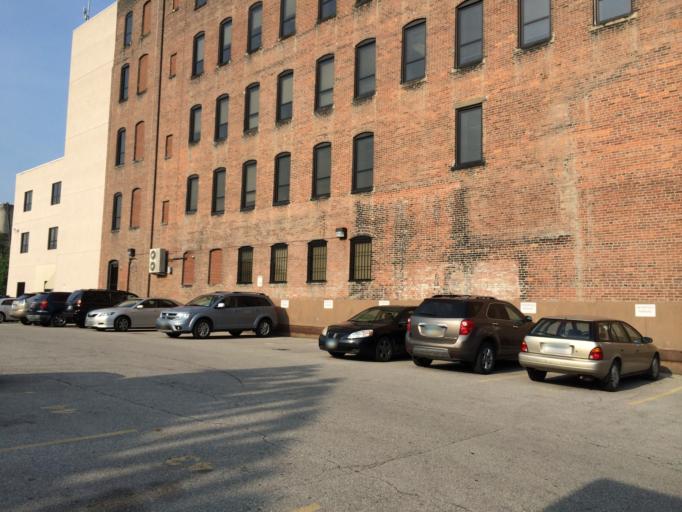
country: US
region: Ohio
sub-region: Franklin County
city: Columbus
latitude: 39.9563
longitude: -82.9975
